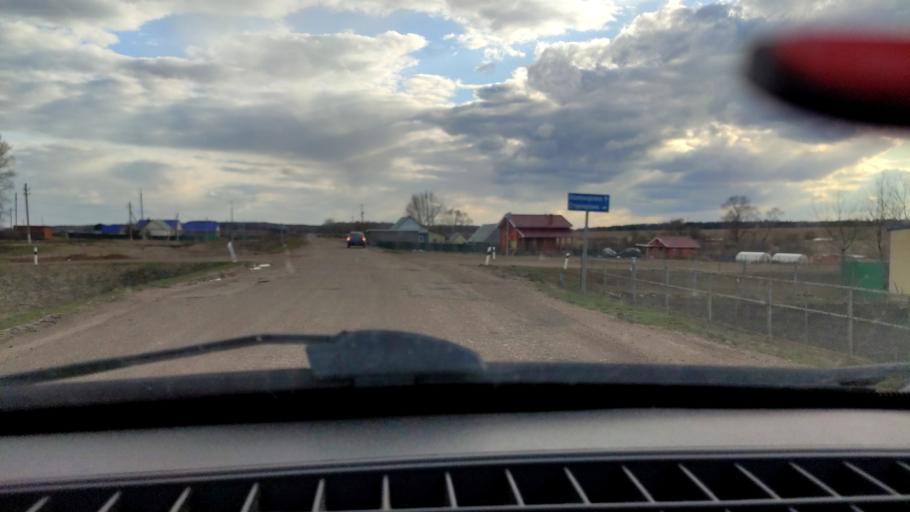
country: RU
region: Bashkortostan
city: Karmaskaly
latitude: 54.3329
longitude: 55.9944
